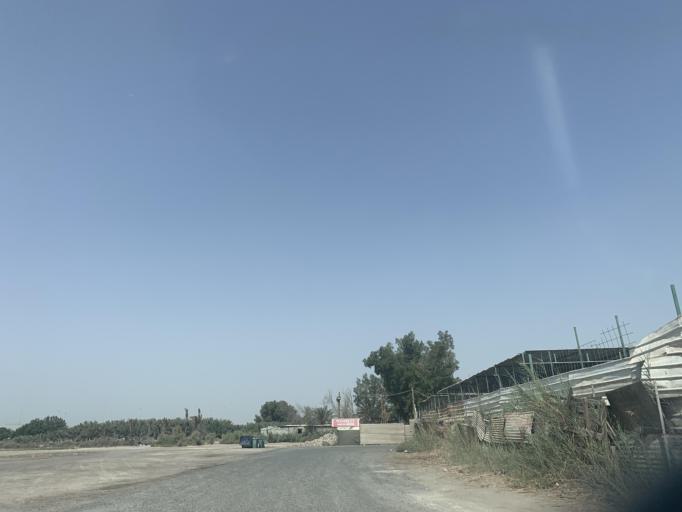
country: BH
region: Manama
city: Jidd Hafs
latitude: 26.2008
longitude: 50.5418
